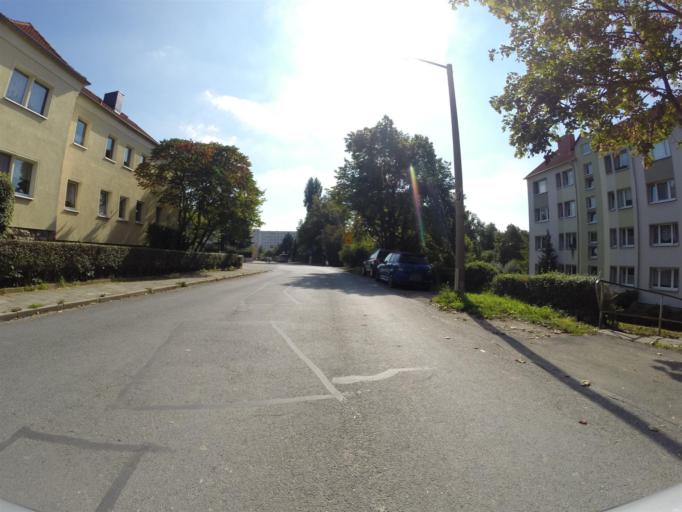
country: DE
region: Thuringia
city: Sulza
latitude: 50.8916
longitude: 11.6092
